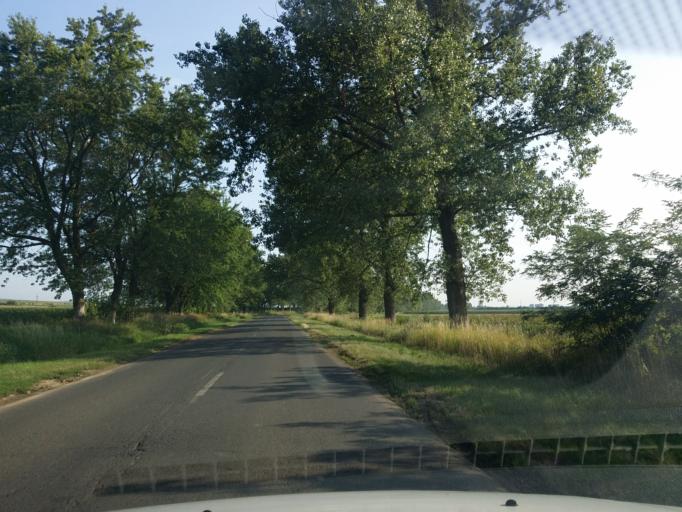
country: HU
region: Borsod-Abauj-Zemplen
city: Gonc
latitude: 48.4054
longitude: 21.2293
